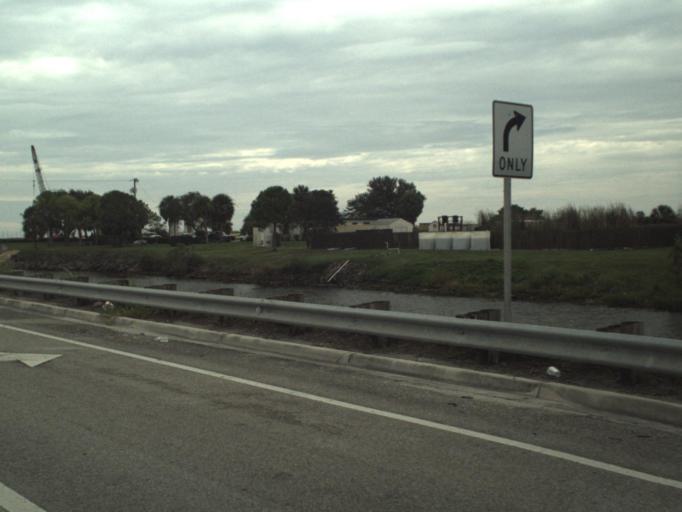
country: US
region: Florida
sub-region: Palm Beach County
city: Loxahatchee Groves
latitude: 26.6851
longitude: -80.3665
